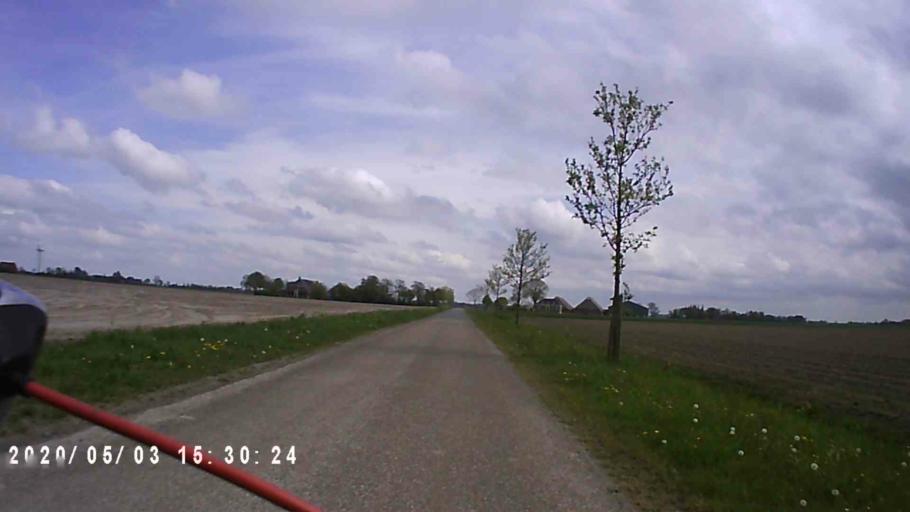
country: NL
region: Groningen
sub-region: Gemeente Winsum
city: Winsum
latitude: 53.3463
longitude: 6.4642
